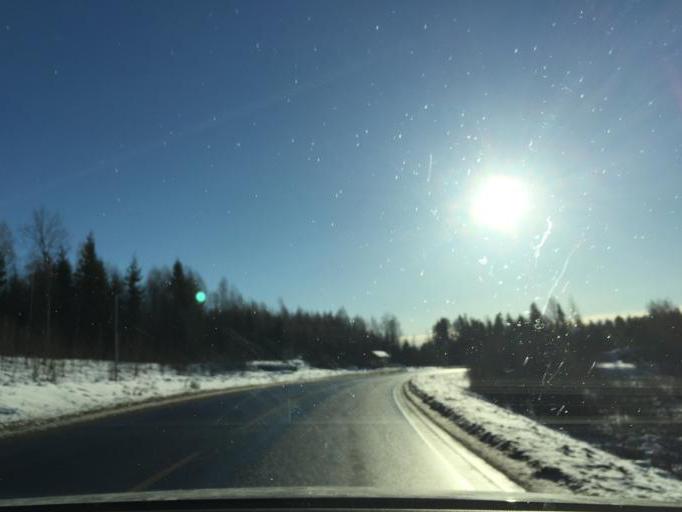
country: NO
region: Akershus
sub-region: Nes
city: Arnes
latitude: 60.1778
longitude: 11.5371
